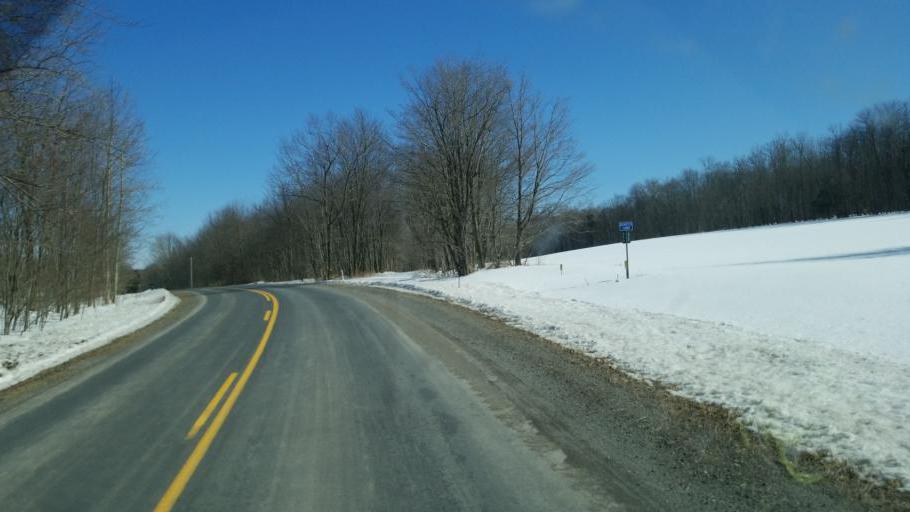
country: US
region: New York
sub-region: Allegany County
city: Andover
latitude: 42.0947
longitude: -77.7156
